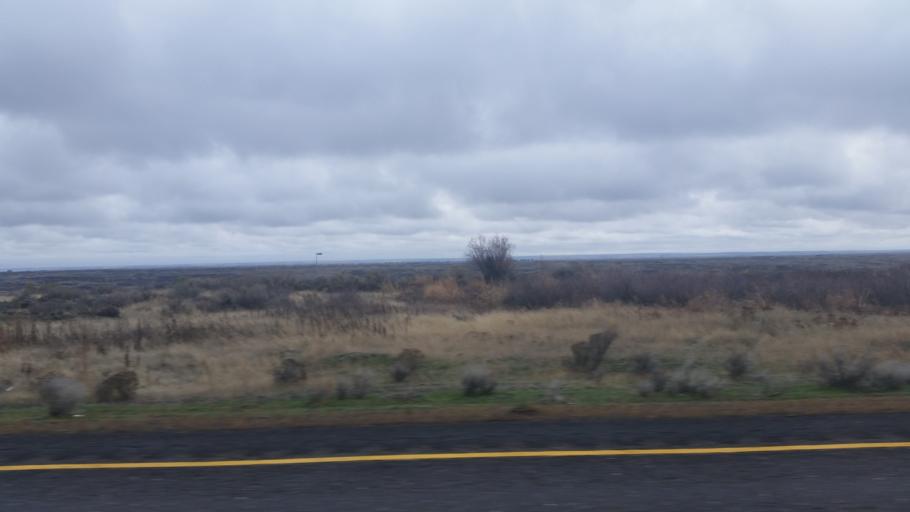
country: US
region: Washington
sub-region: Lincoln County
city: Davenport
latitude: 47.2920
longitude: -118.0345
